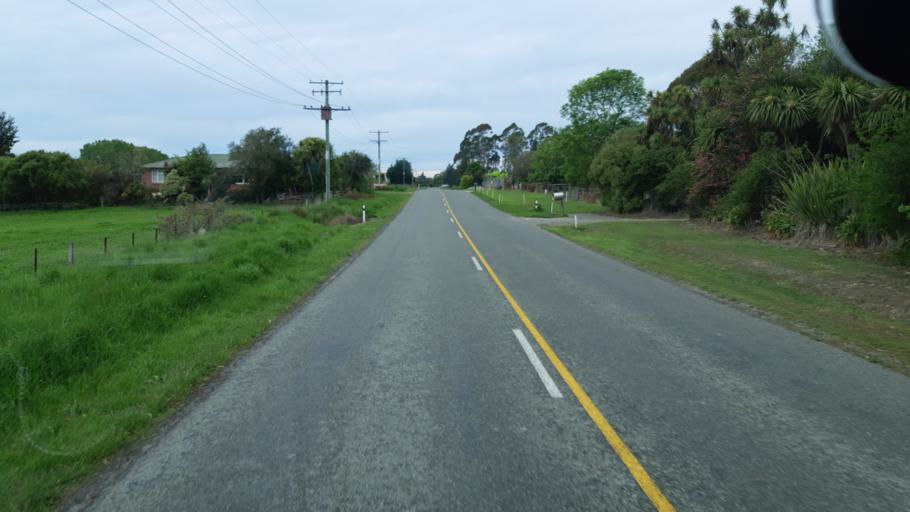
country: NZ
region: Canterbury
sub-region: Timaru District
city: Timaru
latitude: -44.4132
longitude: 171.1951
